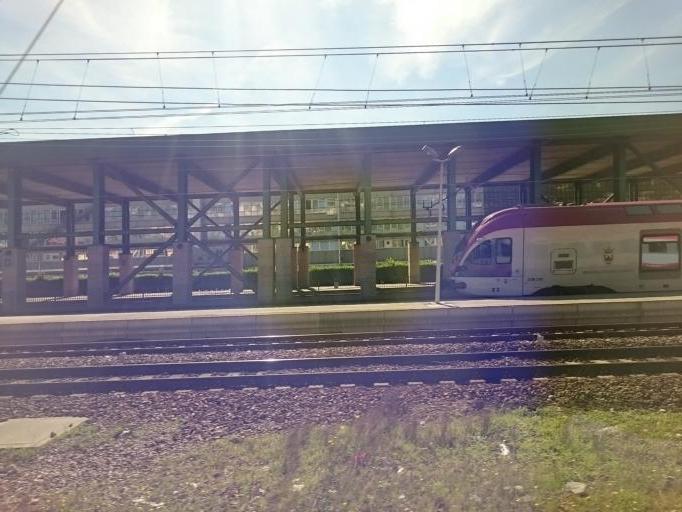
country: IT
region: Trentino-Alto Adige
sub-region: Provincia di Trento
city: Trento
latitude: 46.0747
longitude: 11.1207
